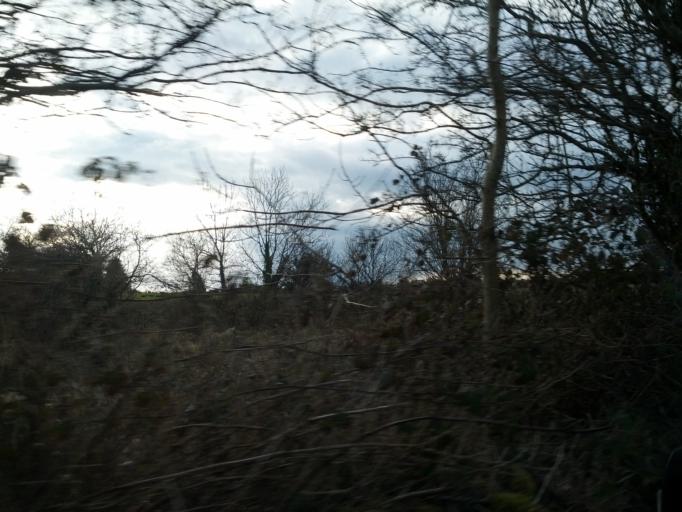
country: IE
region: Connaught
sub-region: County Galway
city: Athenry
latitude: 53.3518
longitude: -8.6665
